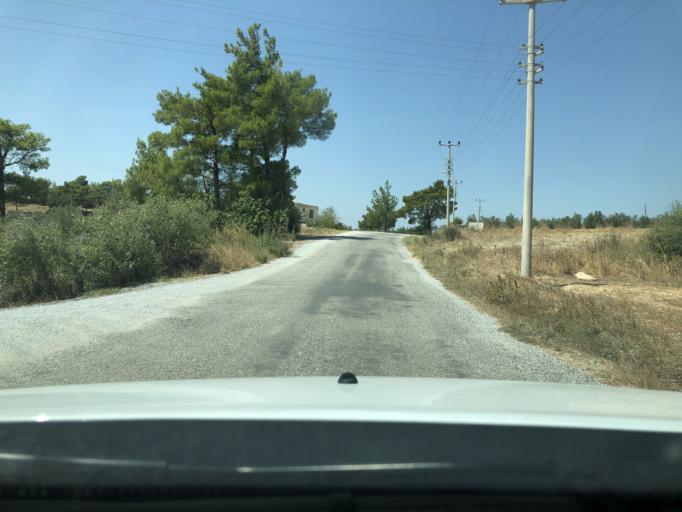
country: TR
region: Antalya
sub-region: Manavgat
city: Kizilagac
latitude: 36.8560
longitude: 31.5652
